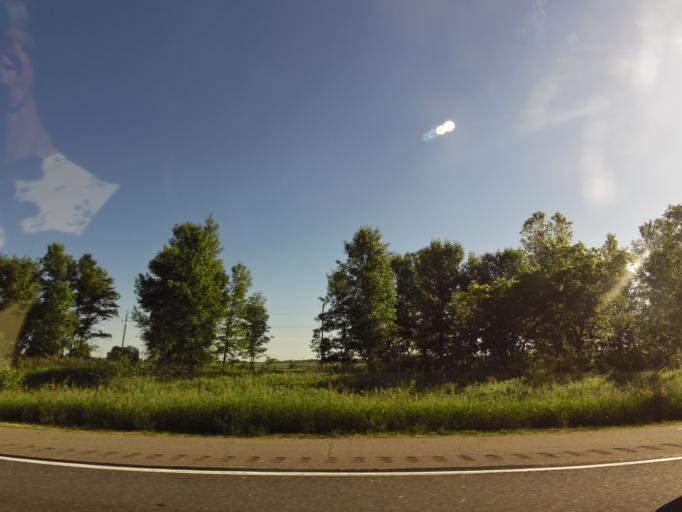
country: US
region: Minnesota
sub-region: Stearns County
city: Albany
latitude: 45.6562
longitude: -94.6739
